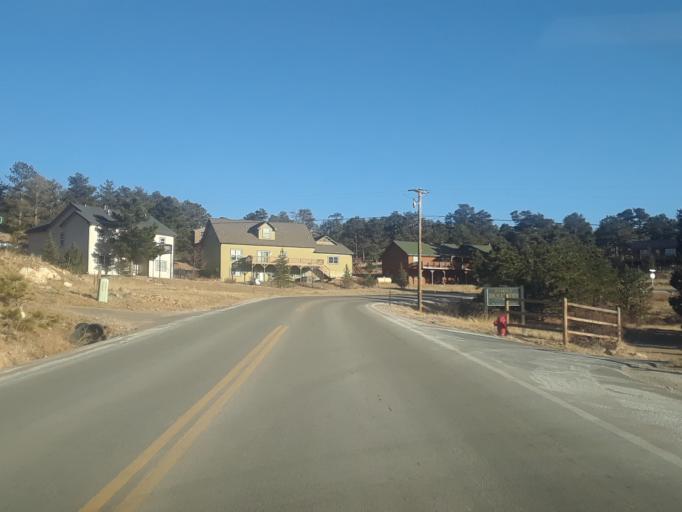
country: US
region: Colorado
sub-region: Larimer County
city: Estes Park
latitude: 40.3509
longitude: -105.5399
